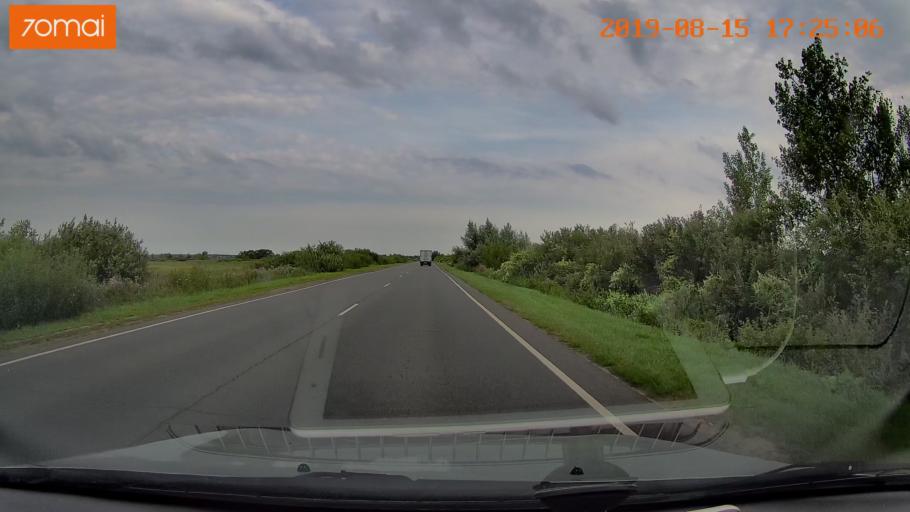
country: RU
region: Moskovskaya
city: Ashitkovo
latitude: 55.3787
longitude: 38.5619
